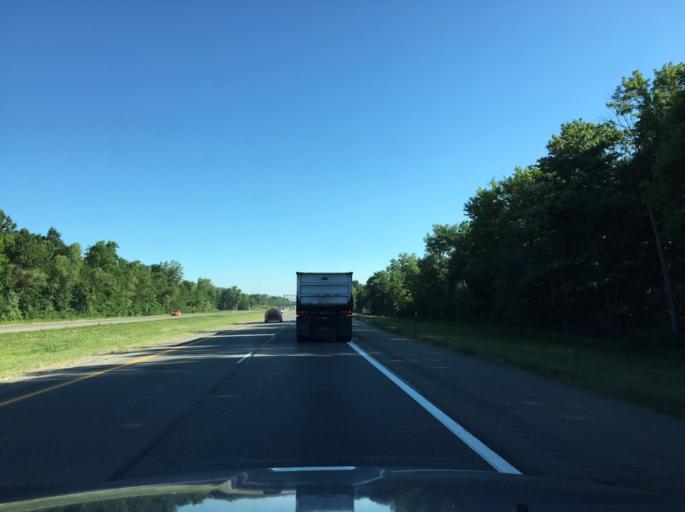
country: US
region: Michigan
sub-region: Macomb County
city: Shelby
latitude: 42.6628
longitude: -83.0143
